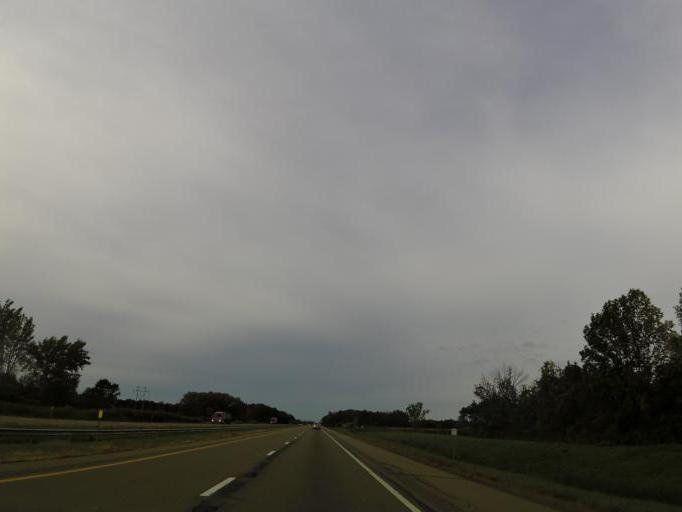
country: US
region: New York
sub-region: Chautauqua County
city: Dunkirk
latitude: 42.4775
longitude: -79.2691
